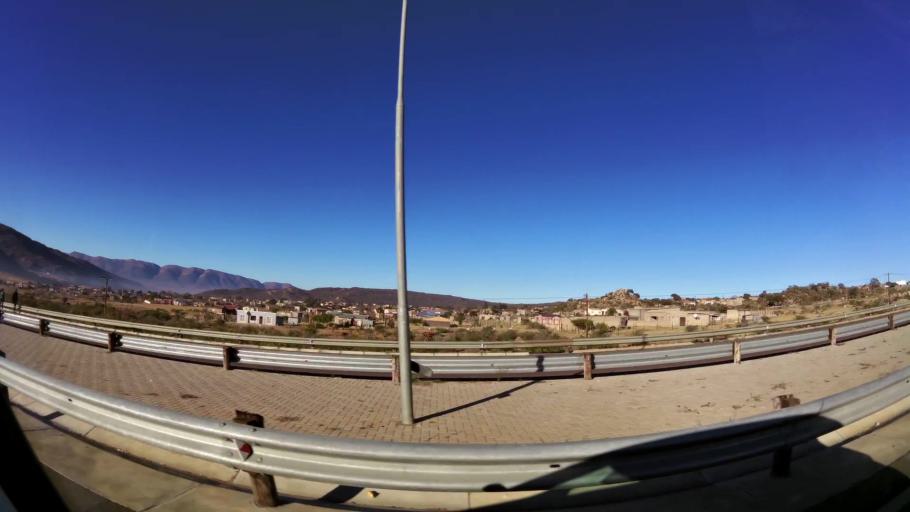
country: ZA
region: Limpopo
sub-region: Capricorn District Municipality
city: Mankoeng
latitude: -23.9140
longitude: 29.7867
